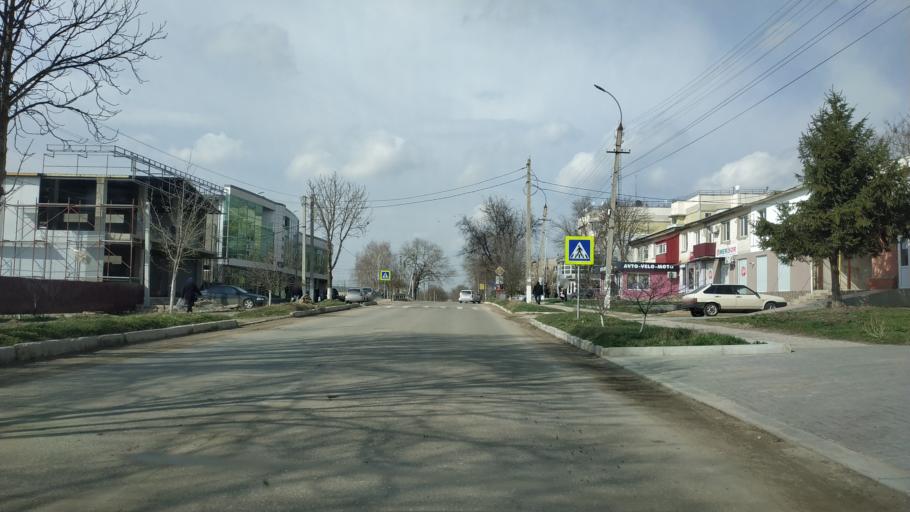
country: MD
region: Gagauzia
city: Vulcanesti
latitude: 45.6865
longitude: 28.4043
